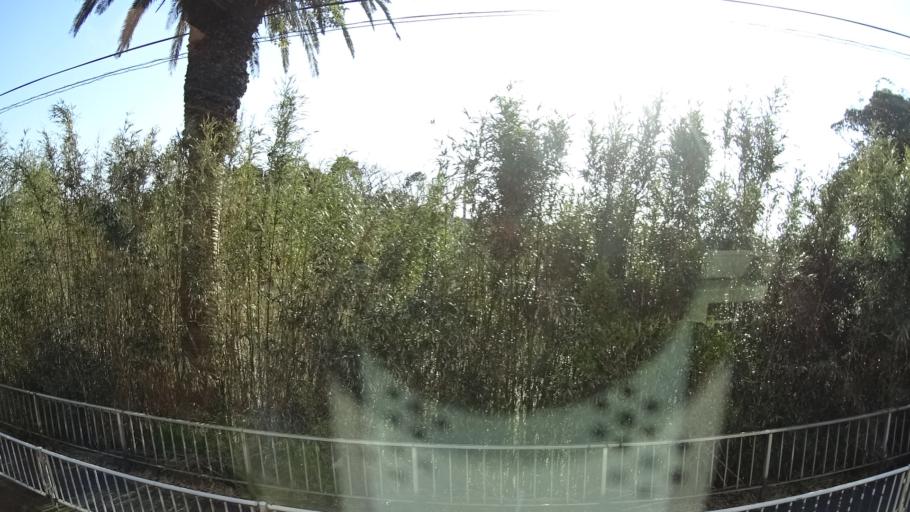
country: JP
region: Kanagawa
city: Miura
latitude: 35.1577
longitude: 139.6288
